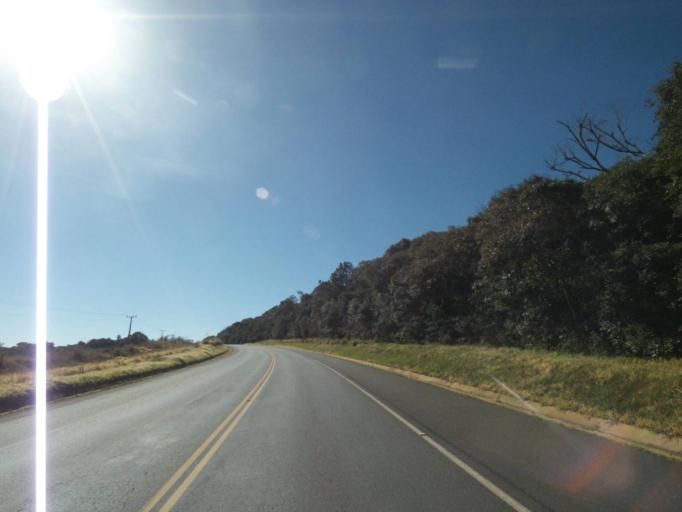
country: BR
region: Parana
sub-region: Tibagi
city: Tibagi
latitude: -24.3765
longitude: -50.3265
